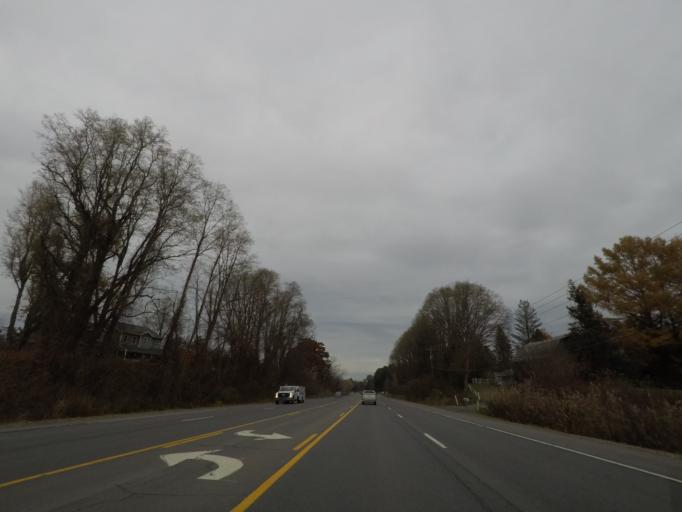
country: US
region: New York
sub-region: Saratoga County
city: Country Knolls
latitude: 42.8956
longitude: -73.7722
